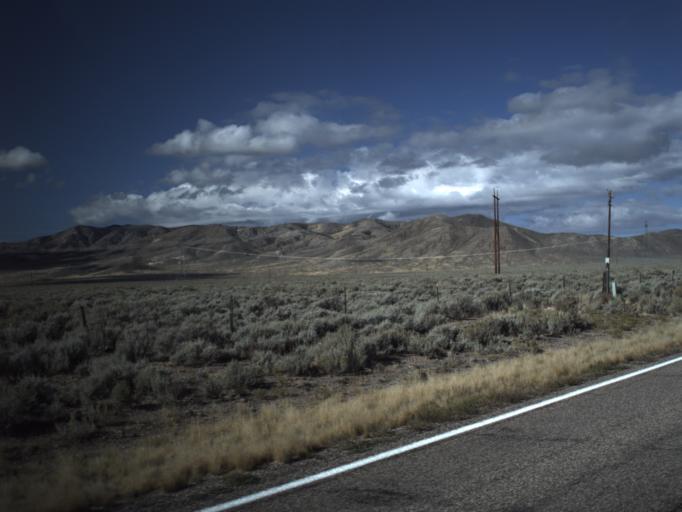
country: US
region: Utah
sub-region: Beaver County
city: Milford
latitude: 38.4078
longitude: -113.0549
